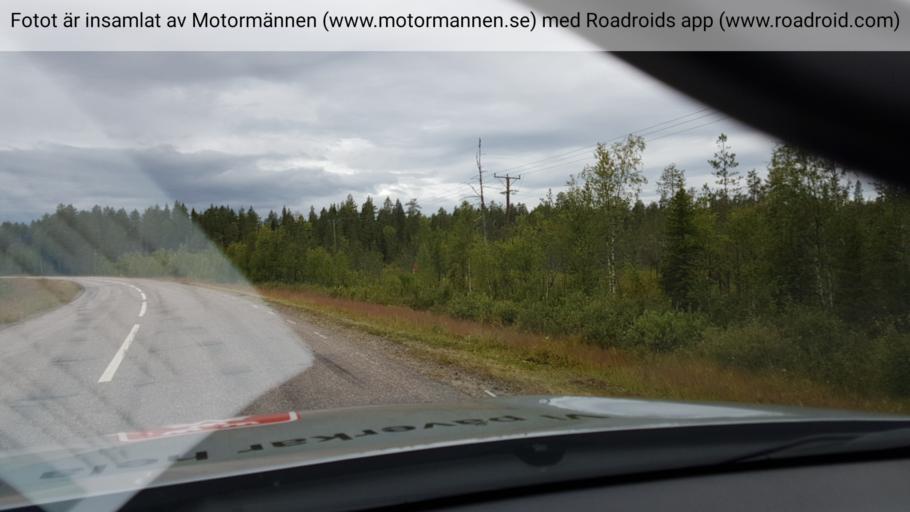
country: SE
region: Norrbotten
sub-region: Overkalix Kommun
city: OEverkalix
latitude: 66.8009
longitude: 22.9508
